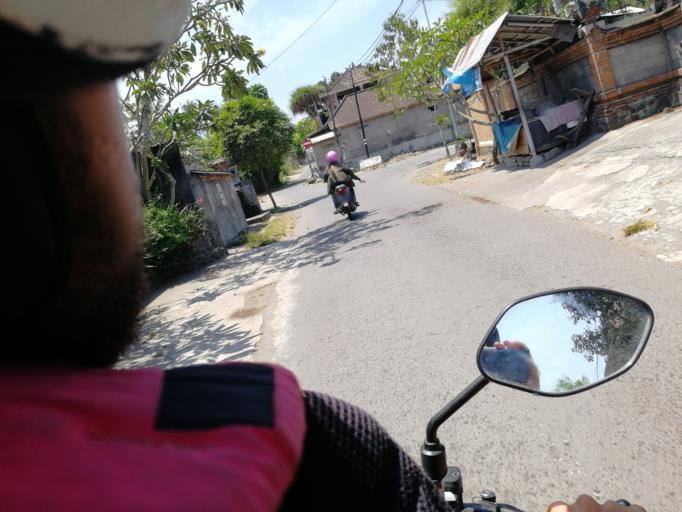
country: ID
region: Bali
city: Subagan
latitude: -8.4586
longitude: 115.5970
